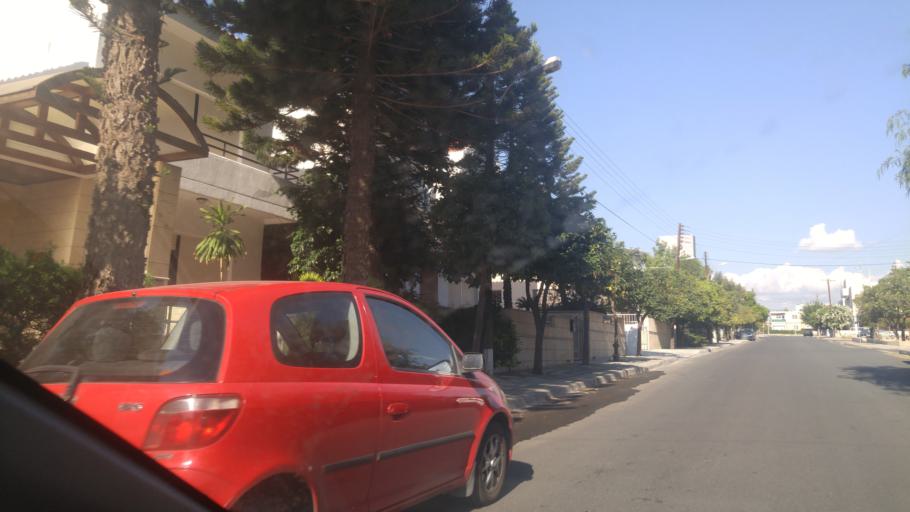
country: CY
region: Limassol
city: Limassol
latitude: 34.6921
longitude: 33.0501
